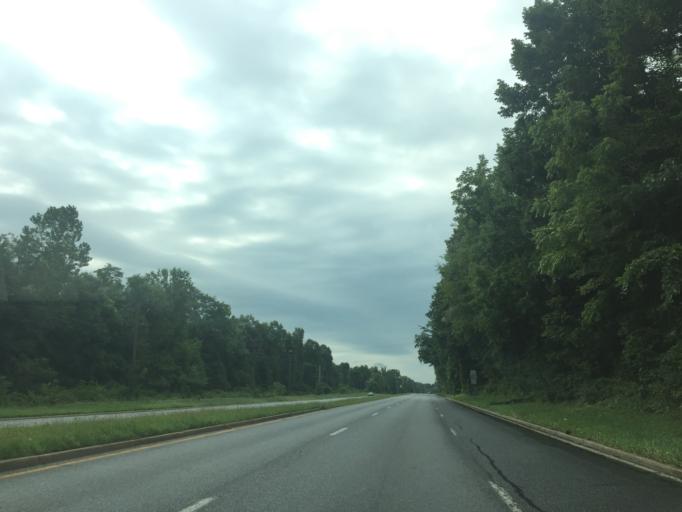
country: US
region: Maryland
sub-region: Baltimore County
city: Woodlawn
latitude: 39.3102
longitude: -76.7162
